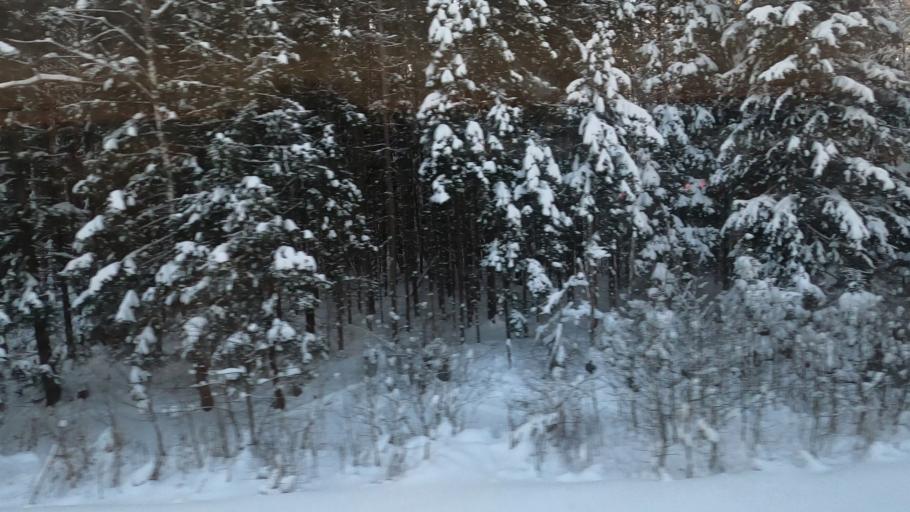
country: RU
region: Moskovskaya
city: Novo-Nikol'skoye
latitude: 56.5998
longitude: 37.5671
